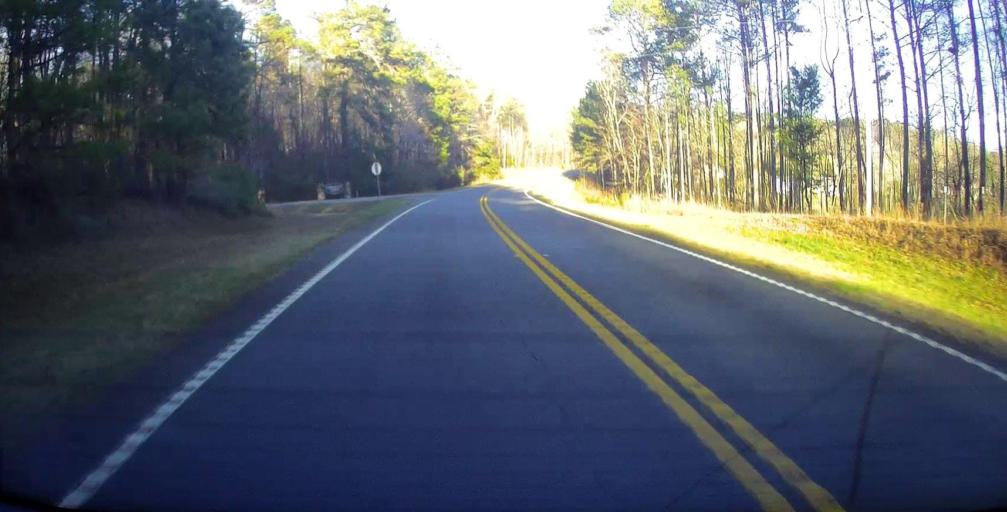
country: US
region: Georgia
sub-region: Talbot County
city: Talbotton
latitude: 32.6601
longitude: -84.6544
